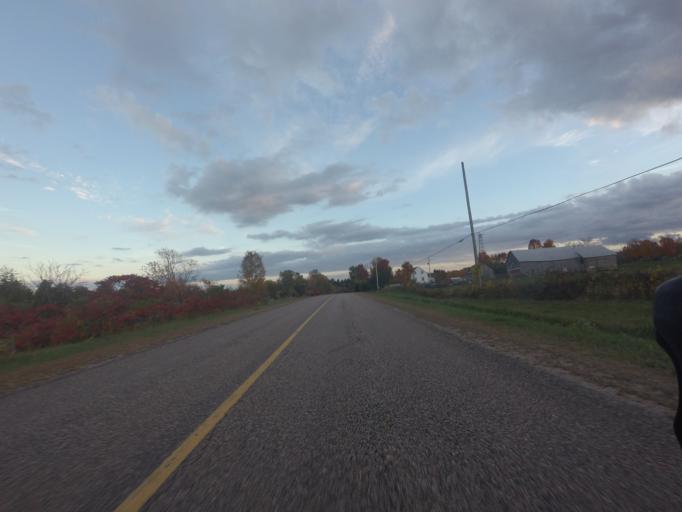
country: CA
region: Ontario
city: Renfrew
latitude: 45.4107
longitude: -76.9530
